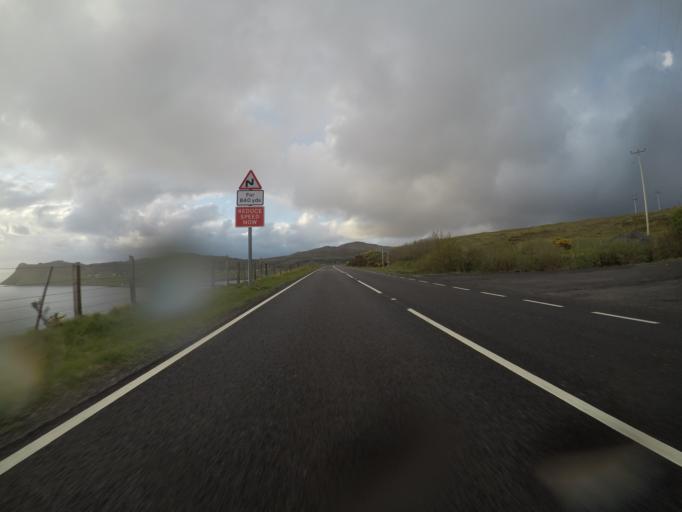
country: GB
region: Scotland
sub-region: Highland
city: Portree
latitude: 57.5758
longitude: -6.3655
